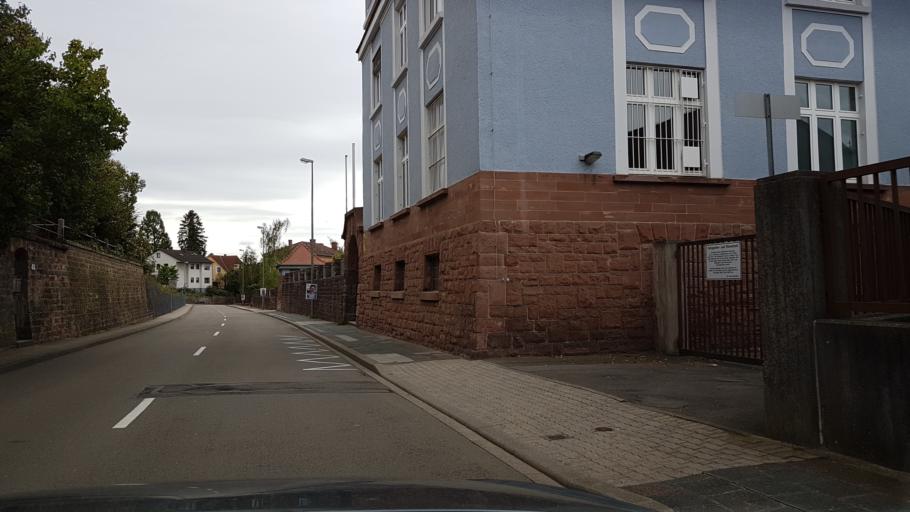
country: DE
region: Rheinland-Pfalz
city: Zweibrucken
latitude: 49.2434
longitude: 7.3728
